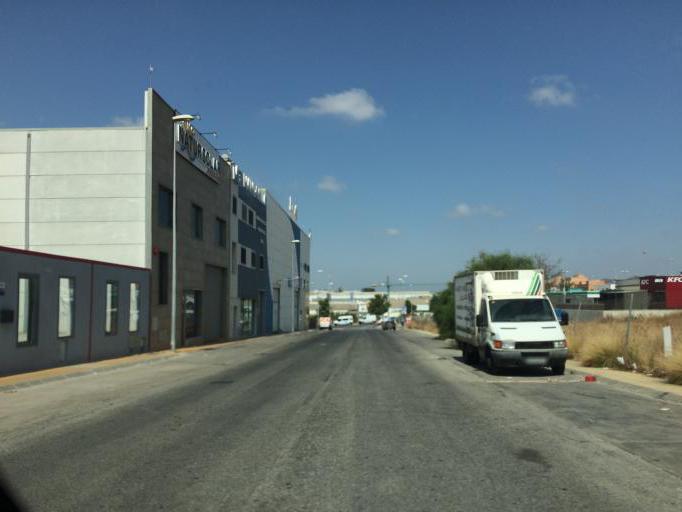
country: ES
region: Andalusia
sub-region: Provincia de Malaga
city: Malaga
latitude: 36.7123
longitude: -4.4708
